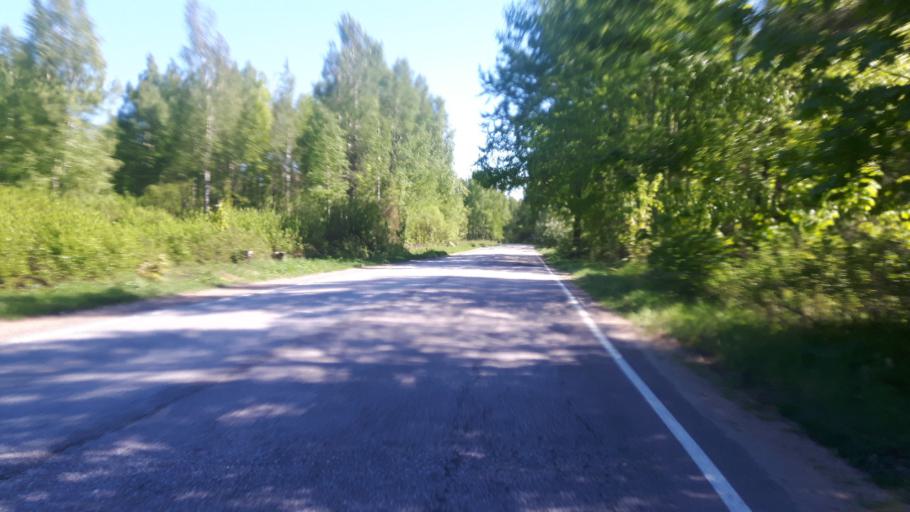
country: RU
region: Leningrad
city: Glebychevo
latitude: 60.2834
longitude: 28.8800
